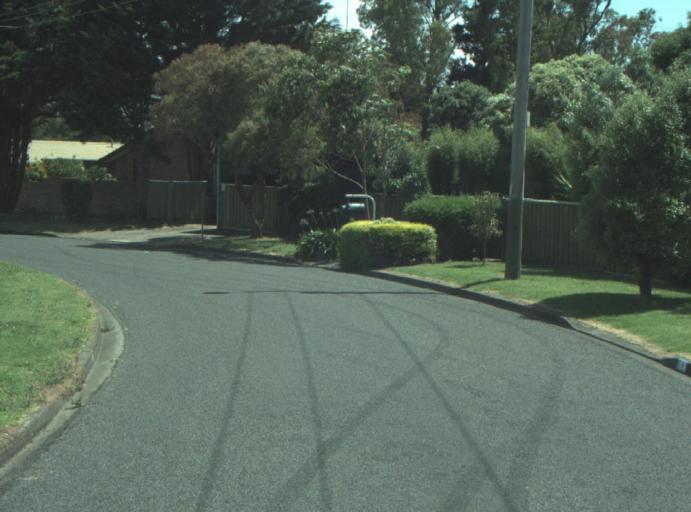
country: AU
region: Victoria
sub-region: Greater Geelong
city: Clifton Springs
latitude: -38.1547
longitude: 144.5760
